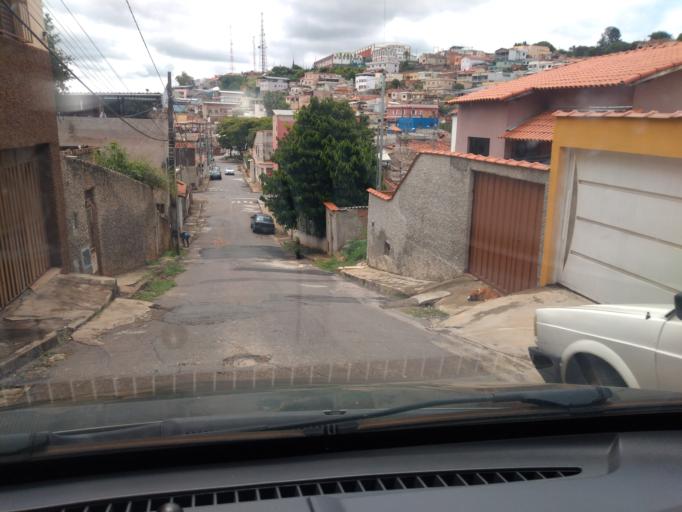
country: BR
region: Minas Gerais
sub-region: Tres Coracoes
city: Tres Coracoes
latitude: -21.6912
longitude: -45.2541
